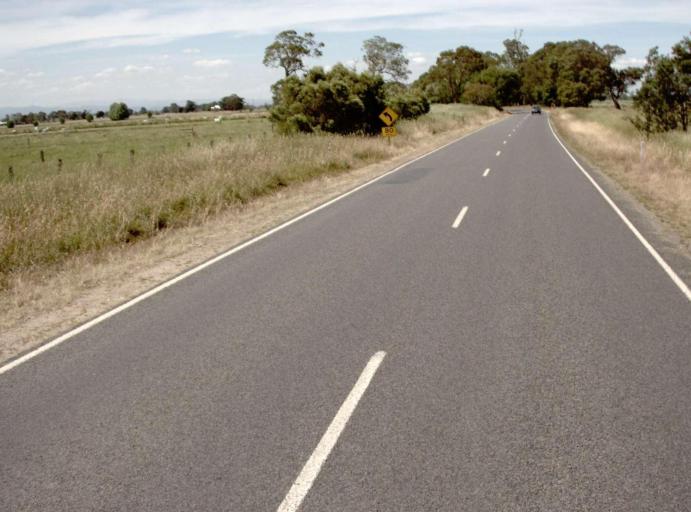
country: AU
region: Victoria
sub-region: Wellington
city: Heyfield
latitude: -38.0070
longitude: 146.8812
